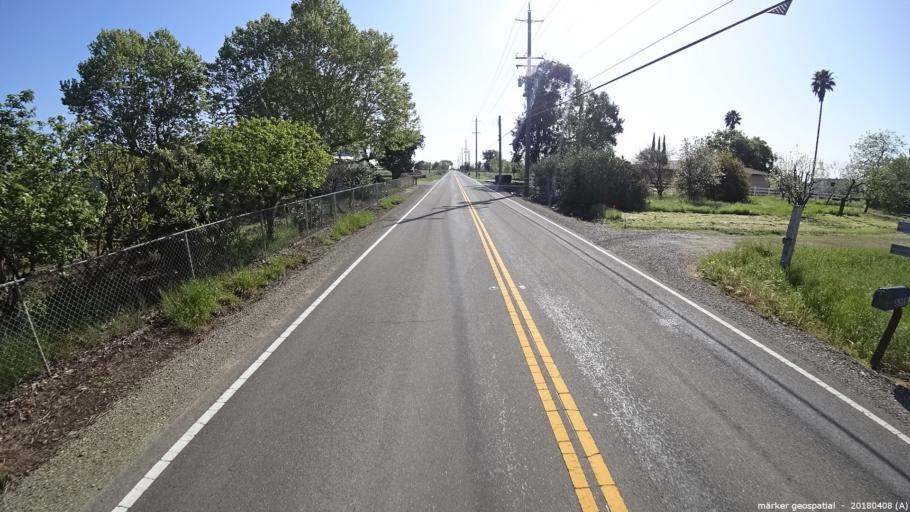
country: US
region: California
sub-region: Sacramento County
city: Elk Grove
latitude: 38.3724
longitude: -121.4073
